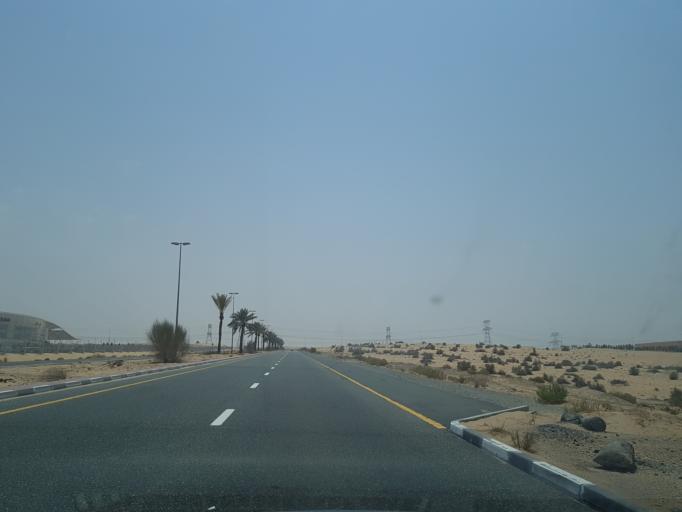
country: AE
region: Ash Shariqah
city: Sharjah
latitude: 25.1080
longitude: 55.4105
